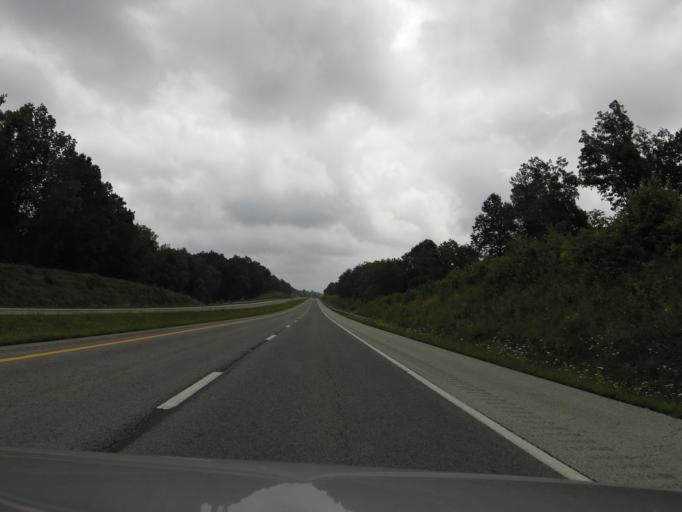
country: US
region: Kentucky
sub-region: Ohio County
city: Oak Grove
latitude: 37.3934
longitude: -86.7741
